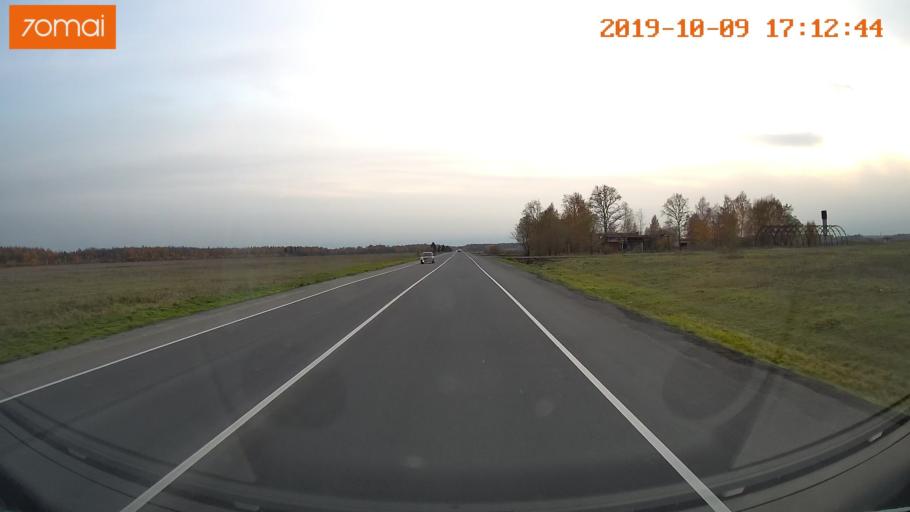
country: RU
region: Ivanovo
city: Privolzhsk
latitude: 57.3246
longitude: 41.2367
